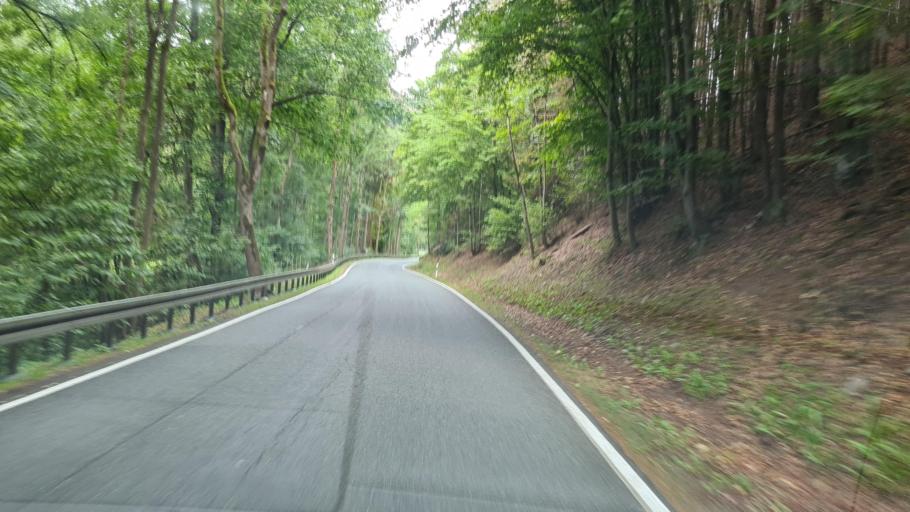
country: DE
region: Thuringia
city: Leutenberg
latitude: 50.5497
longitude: 11.4732
